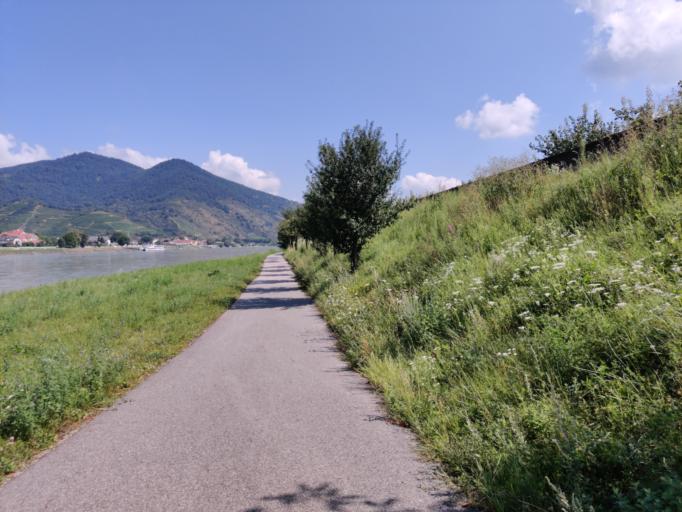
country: AT
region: Lower Austria
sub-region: Politischer Bezirk Krems
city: Spitz
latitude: 48.3557
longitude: 15.4133
